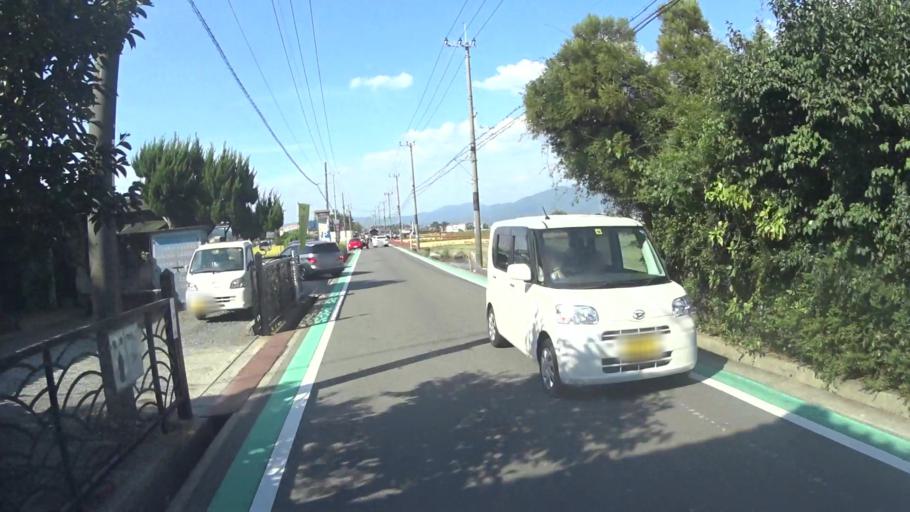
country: JP
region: Kyoto
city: Kameoka
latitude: 34.9996
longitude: 135.5495
